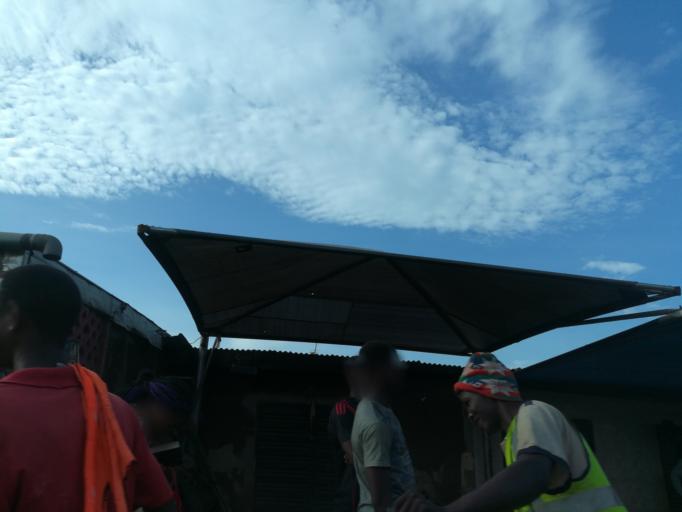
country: NG
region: Lagos
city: Oshodi
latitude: 6.5550
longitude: 3.3314
